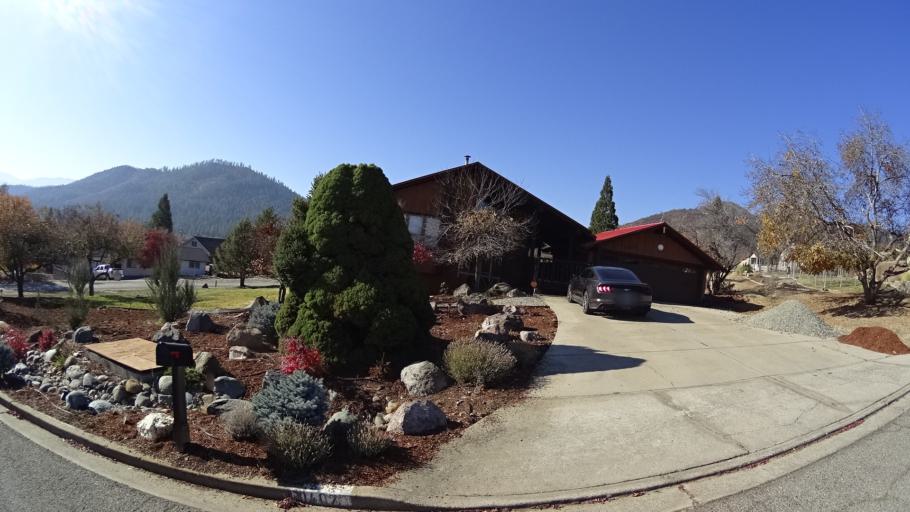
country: US
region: California
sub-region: Siskiyou County
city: Yreka
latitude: 41.7399
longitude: -122.6592
